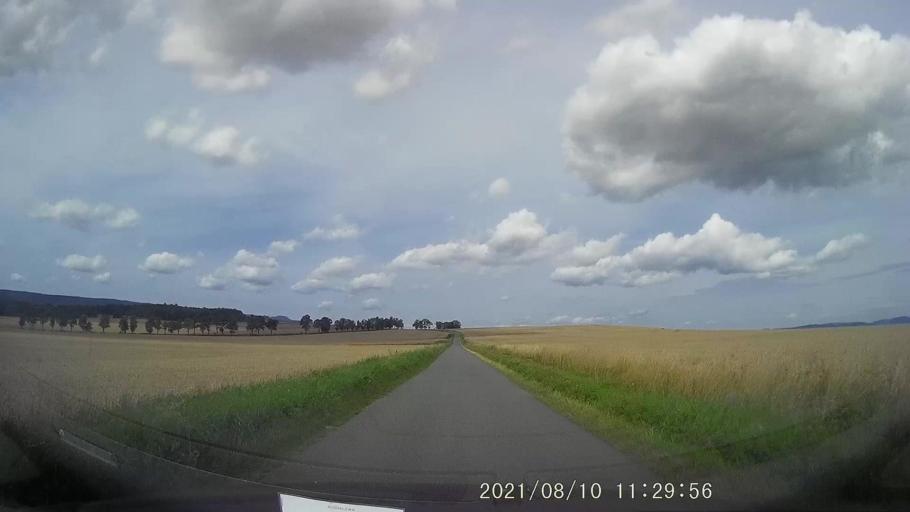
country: PL
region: Lower Silesian Voivodeship
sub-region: Powiat klodzki
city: Polanica-Zdroj
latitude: 50.4474
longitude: 16.5567
